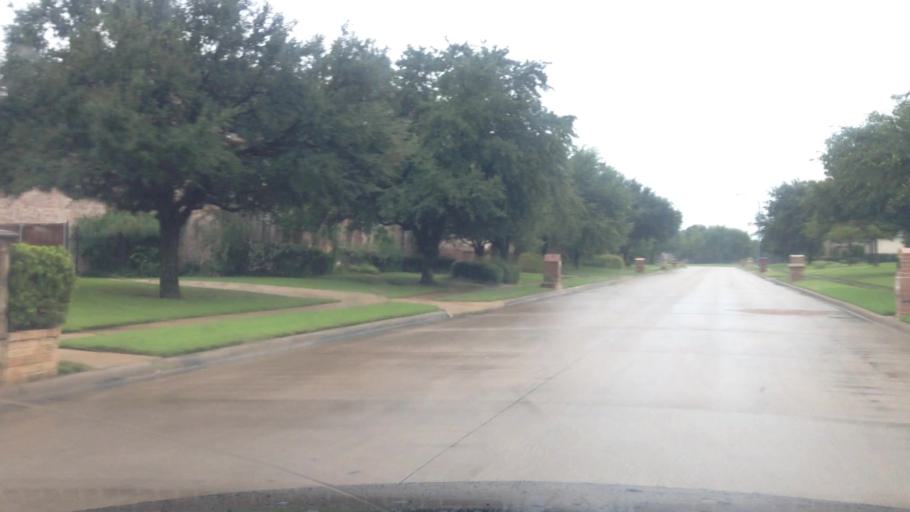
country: US
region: Texas
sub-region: Tarrant County
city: Colleyville
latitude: 32.9006
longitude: -97.1907
